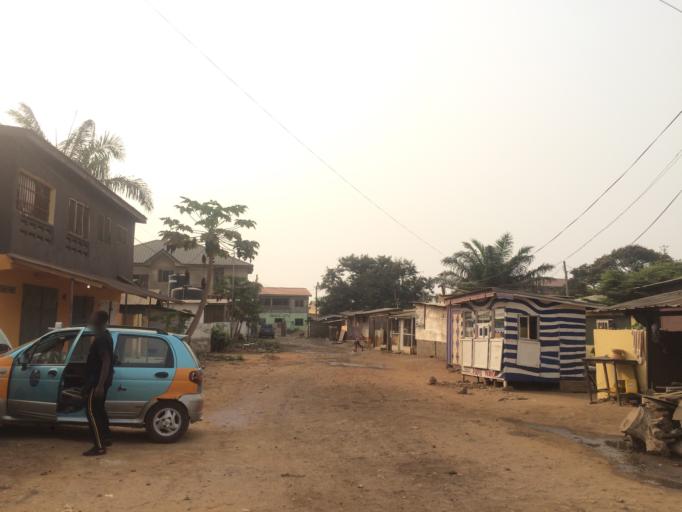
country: GH
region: Greater Accra
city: Nungua
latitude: 5.6039
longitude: -0.0858
